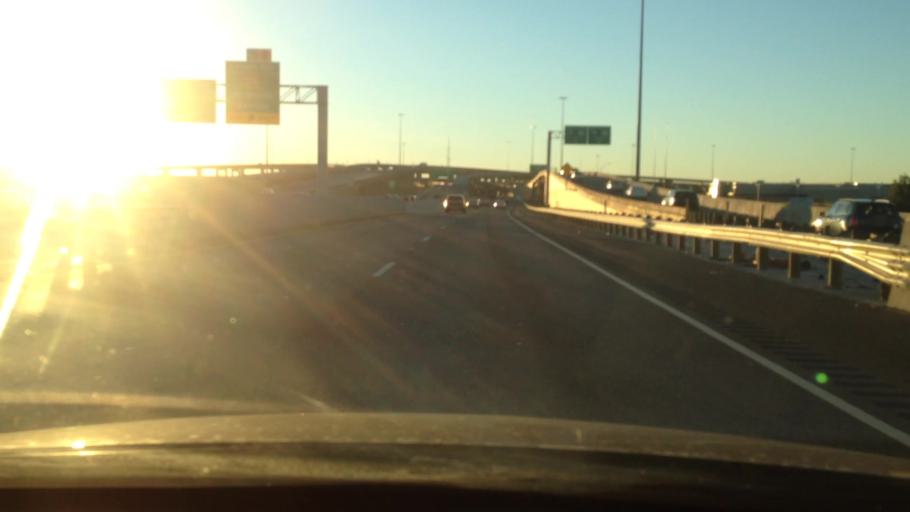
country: US
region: Texas
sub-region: Tarrant County
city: Blue Mound
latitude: 32.8397
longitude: -97.3023
